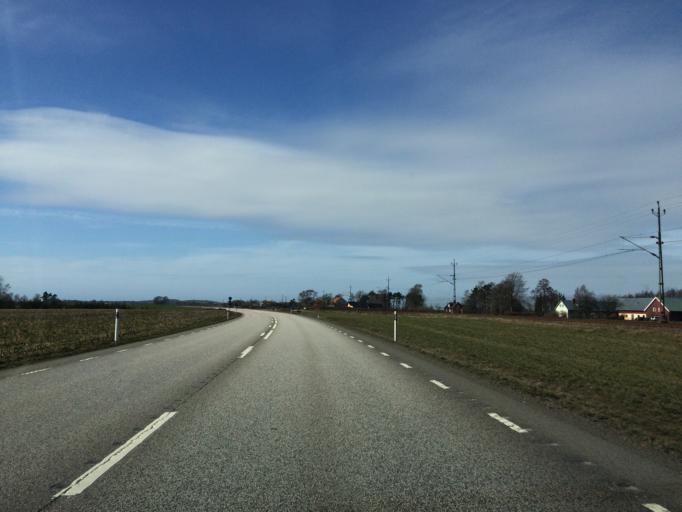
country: SE
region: Halland
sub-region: Laholms Kommun
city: Veinge
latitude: 56.5401
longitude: 13.1517
